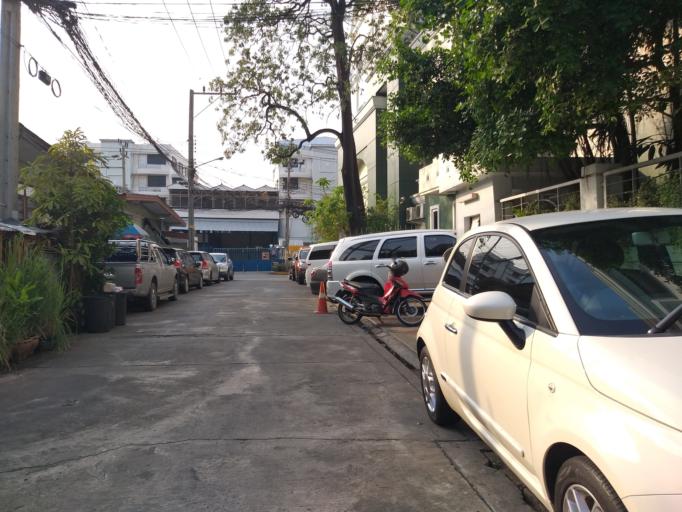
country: TH
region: Bangkok
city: Chatuchak
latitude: 13.8290
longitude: 100.5550
